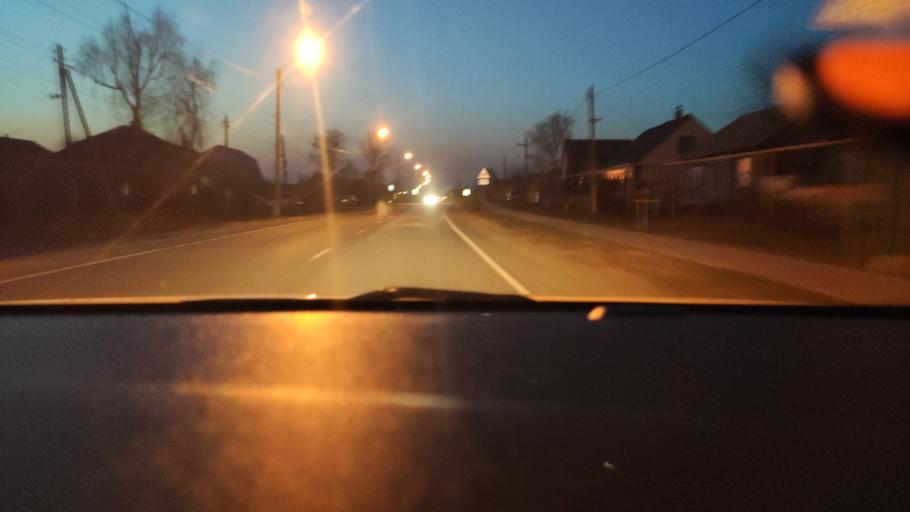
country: RU
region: Voronezj
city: Shilovo
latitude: 51.5582
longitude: 39.0607
